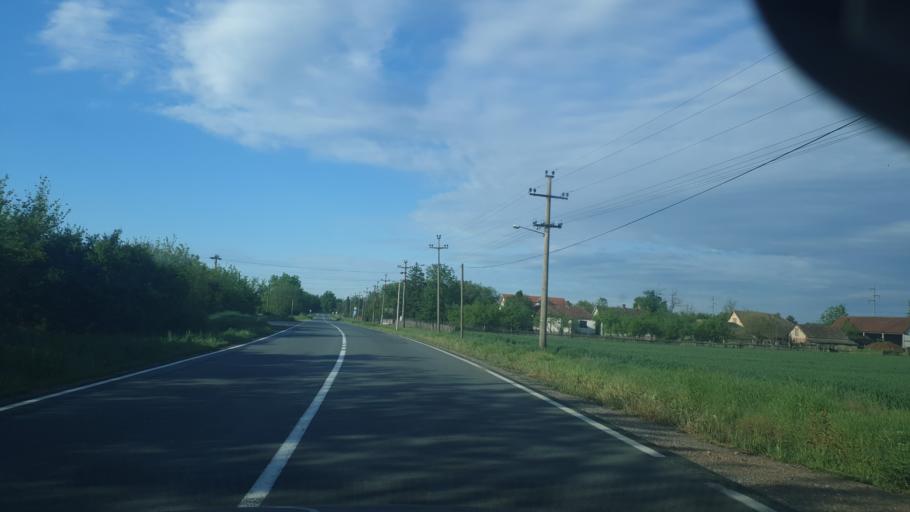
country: RS
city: Stubline
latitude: 44.6024
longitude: 20.1489
